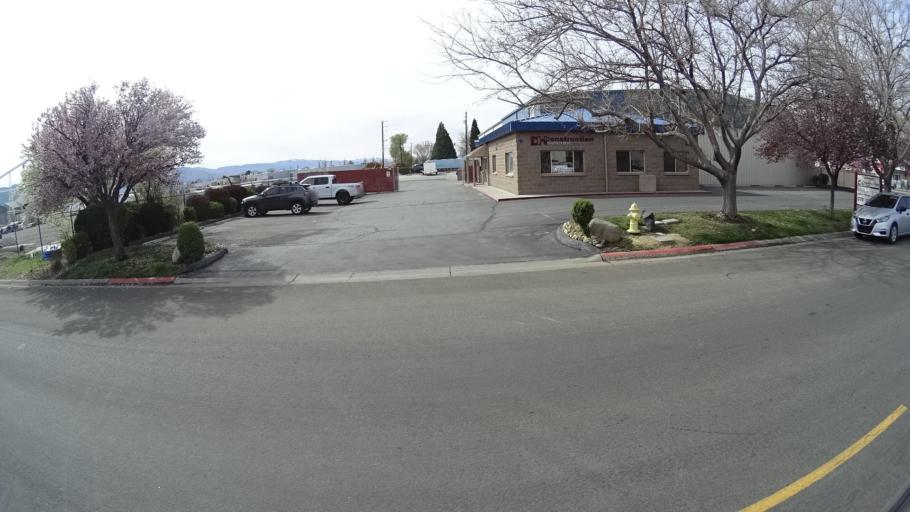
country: US
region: Nevada
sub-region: Washoe County
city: Sparks
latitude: 39.5255
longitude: -119.7569
